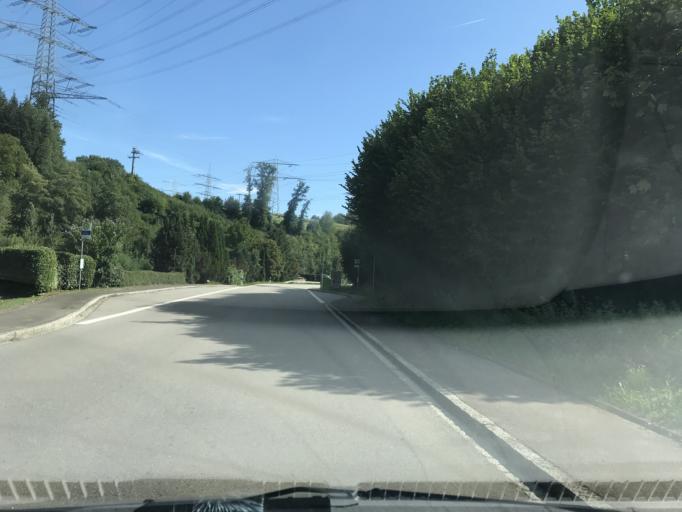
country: DE
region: Baden-Wuerttemberg
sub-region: Freiburg Region
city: Schworstadt
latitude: 47.6045
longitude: 7.8700
